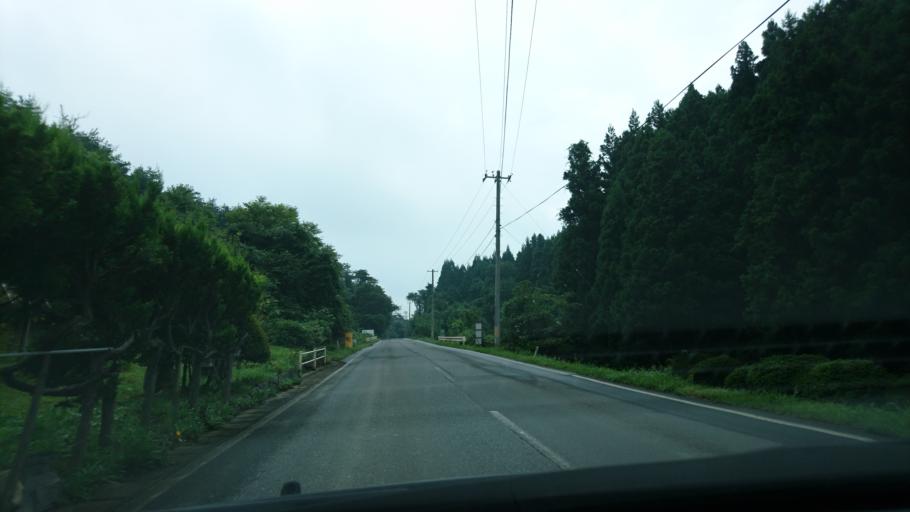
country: JP
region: Iwate
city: Ichinoseki
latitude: 38.9362
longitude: 141.1875
